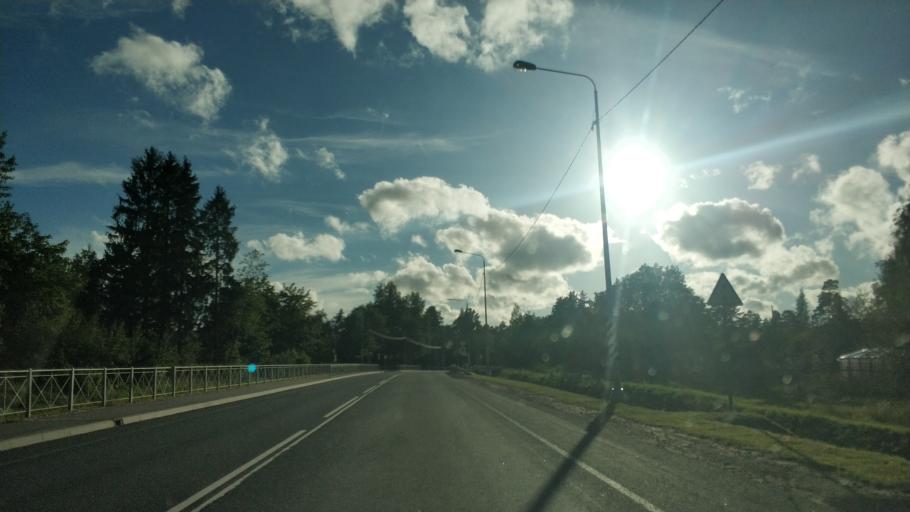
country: RU
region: Leningrad
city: Sapernoye
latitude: 60.7130
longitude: 30.0406
